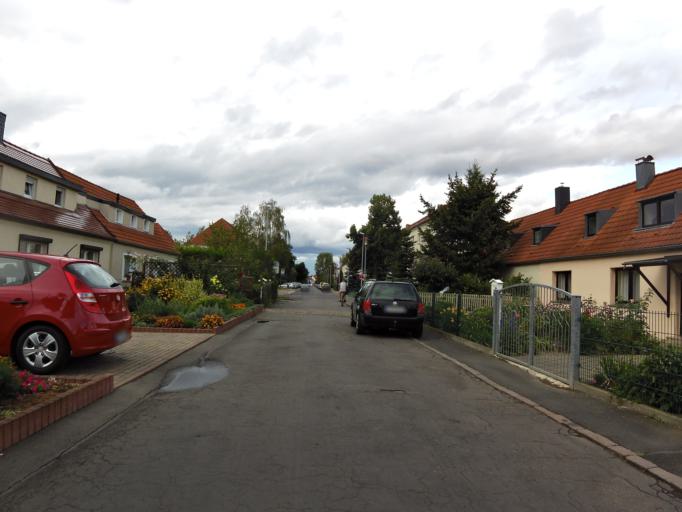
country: DE
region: Saxony
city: Schkeuditz
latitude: 51.3513
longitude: 12.2870
